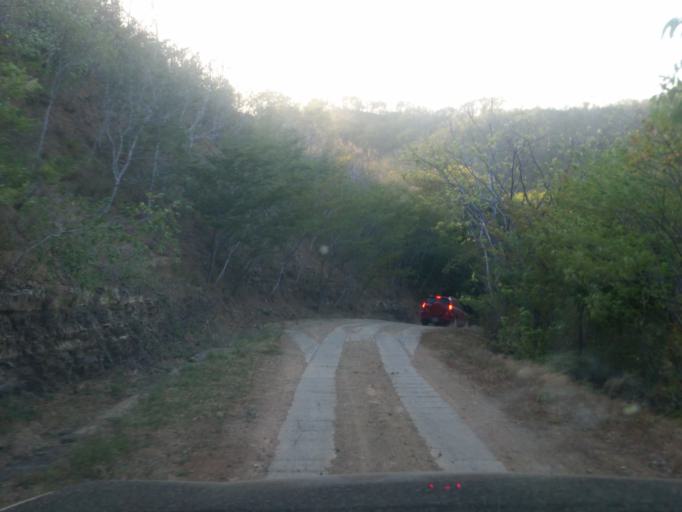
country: NI
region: Rivas
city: San Juan del Sur
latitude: 11.1858
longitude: -85.8124
